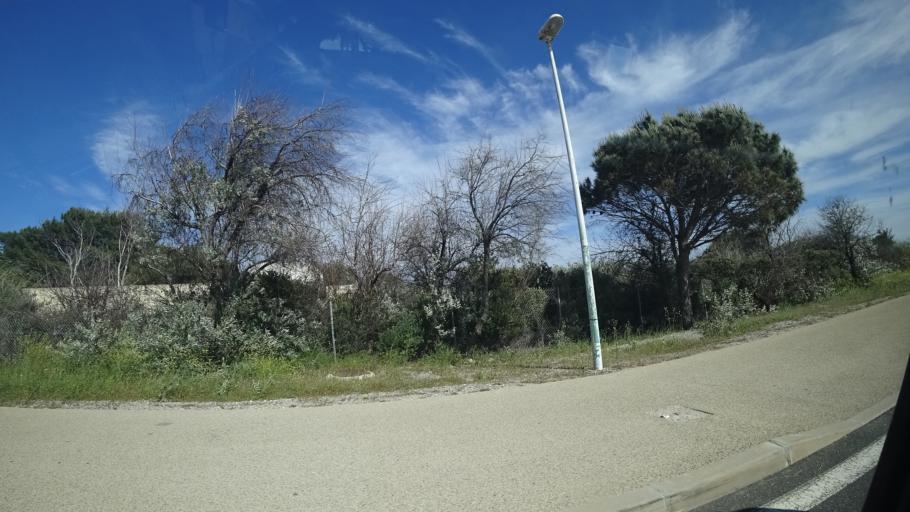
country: FR
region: Languedoc-Roussillon
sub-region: Departement des Pyrenees-Orientales
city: Le Barcares
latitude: 42.8227
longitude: 3.0347
